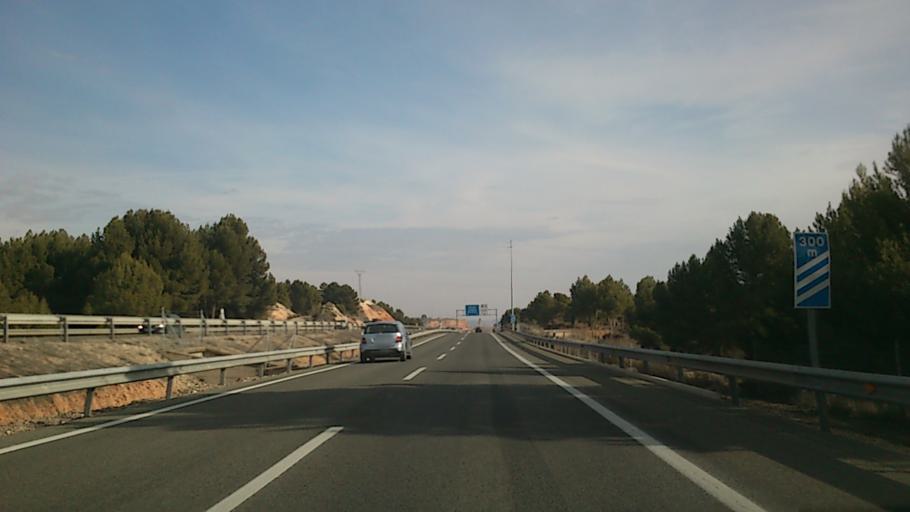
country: ES
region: Aragon
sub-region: Provincia de Zaragoza
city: Monreal de Ariza
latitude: 41.3100
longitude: -2.0867
